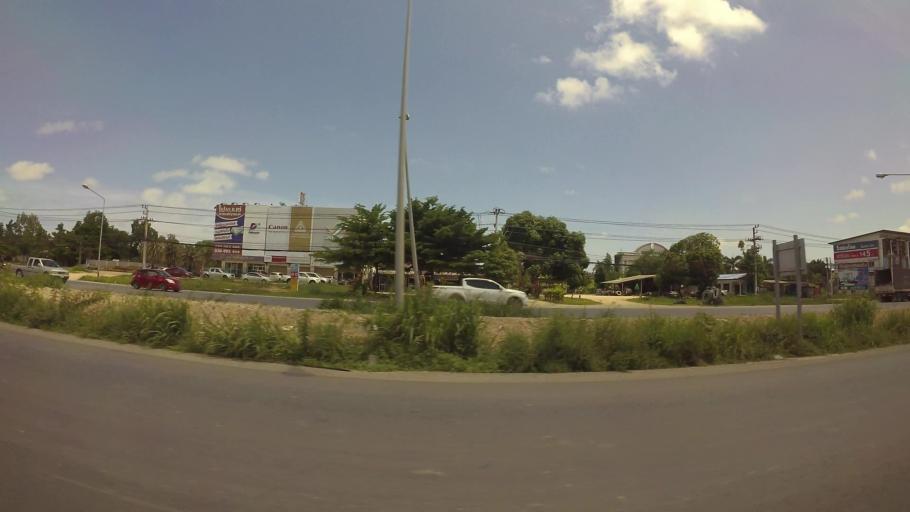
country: TH
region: Rayong
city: Rayong
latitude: 12.7018
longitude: 101.2491
